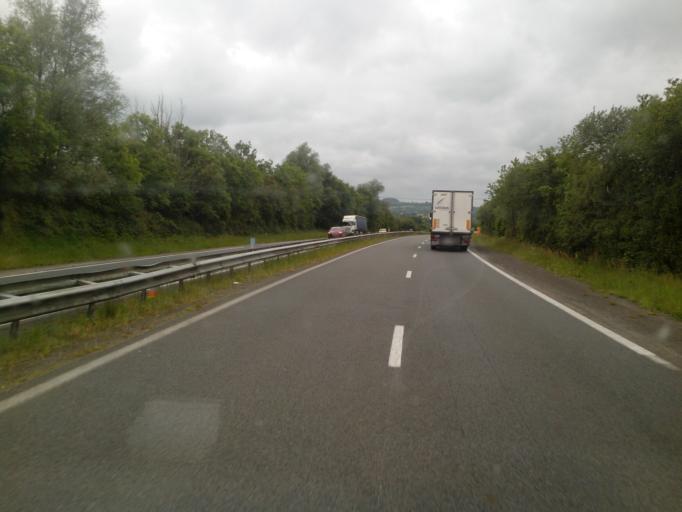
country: FR
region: Brittany
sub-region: Departement des Cotes-d'Armor
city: Pedernec
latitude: 48.5680
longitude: -3.2417
